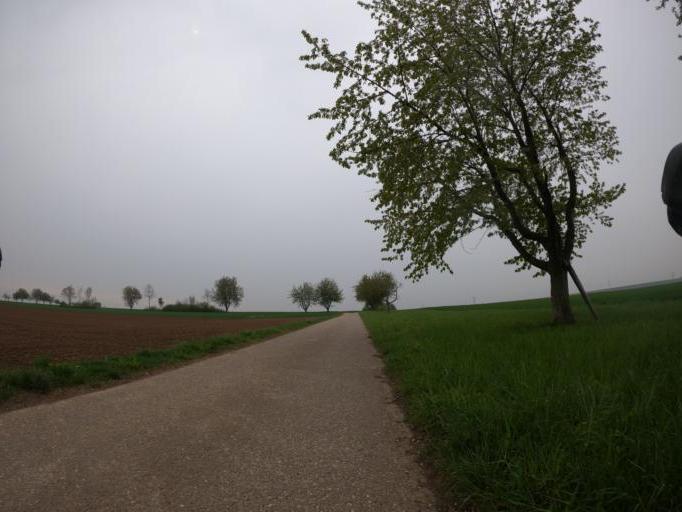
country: DE
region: Baden-Wuerttemberg
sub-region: Regierungsbezirk Stuttgart
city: Sersheim
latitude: 48.9478
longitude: 9.0026
